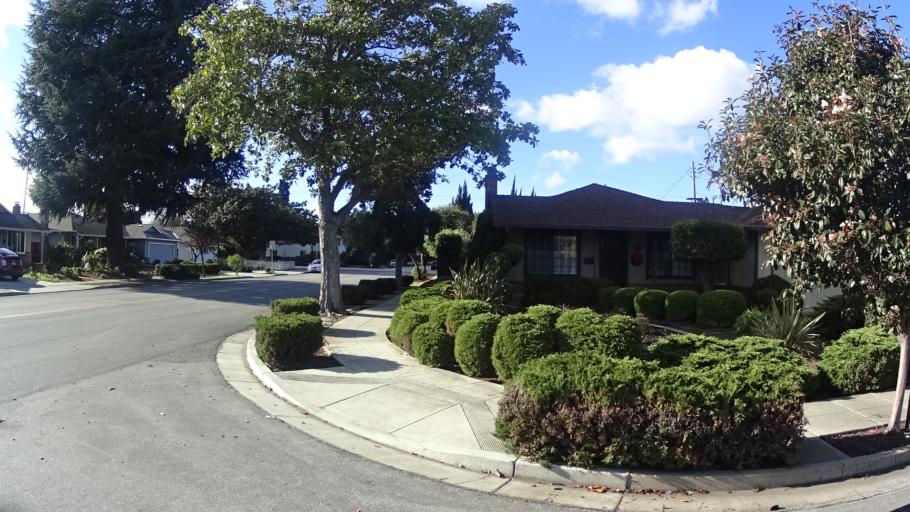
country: US
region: California
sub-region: Santa Clara County
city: Sunnyvale
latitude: 37.3728
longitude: -122.0472
